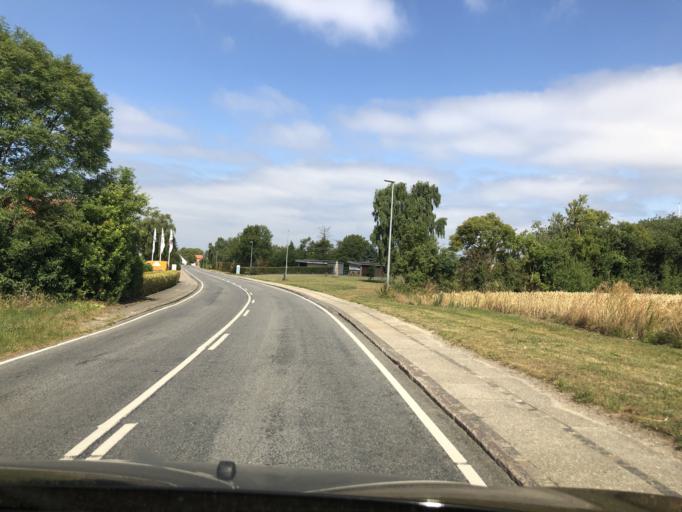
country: DK
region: South Denmark
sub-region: AEro Kommune
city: AEroskobing
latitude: 54.9348
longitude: 10.2635
